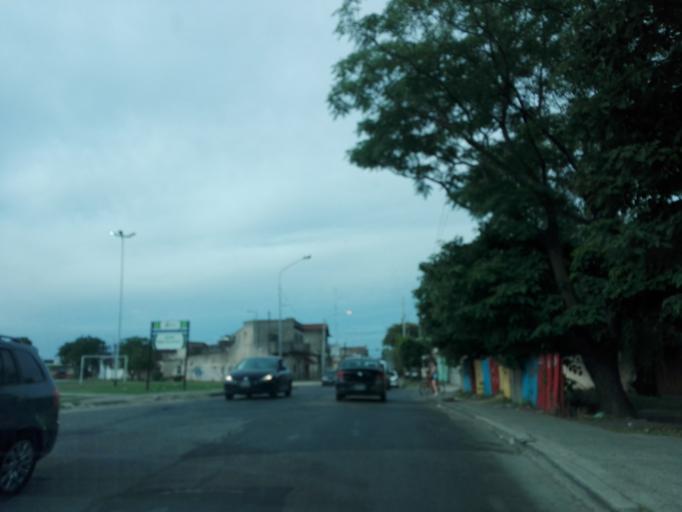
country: AR
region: Buenos Aires
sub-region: Partido de Lanus
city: Lanus
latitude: -34.6961
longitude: -58.3594
